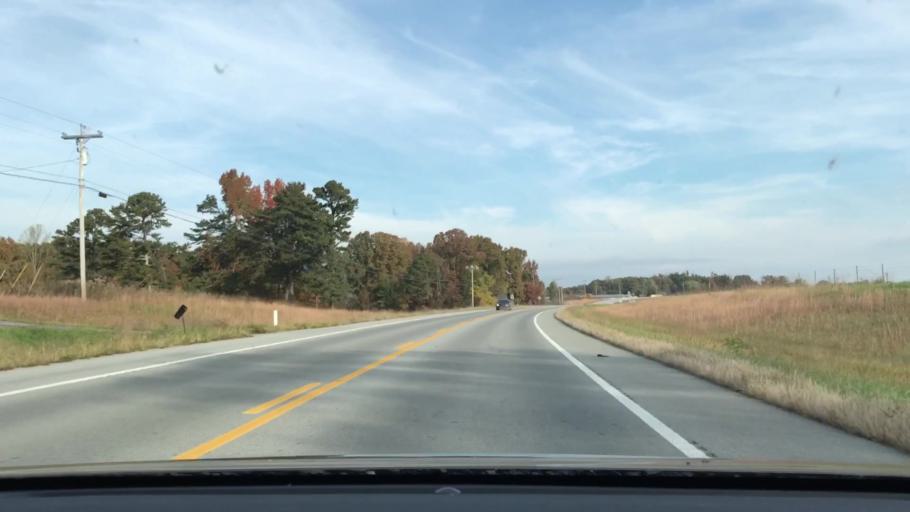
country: US
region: Tennessee
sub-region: Fentress County
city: Grimsley
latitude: 36.3042
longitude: -84.9750
